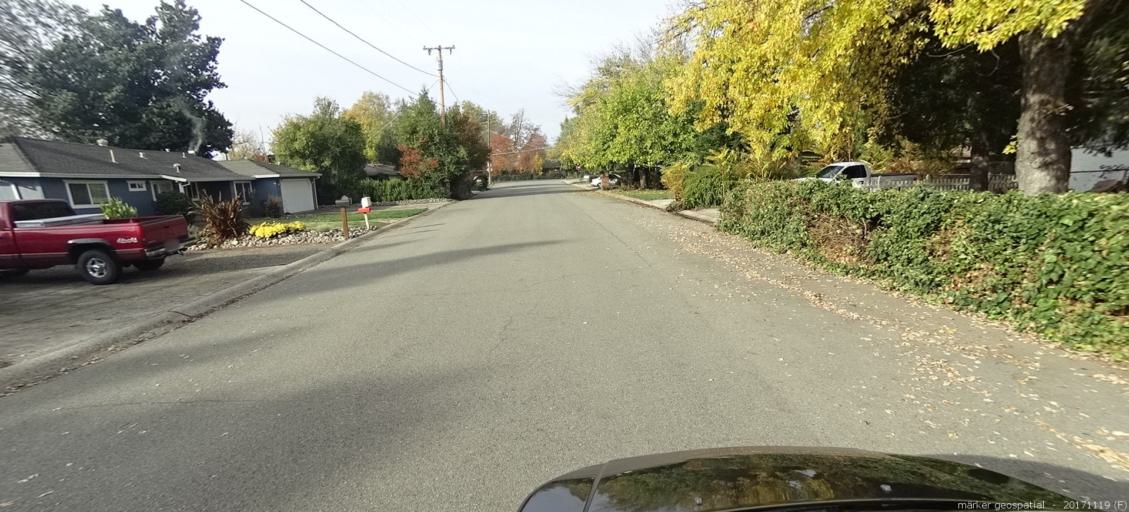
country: US
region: California
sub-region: Shasta County
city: Anderson
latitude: 40.5174
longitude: -122.3323
